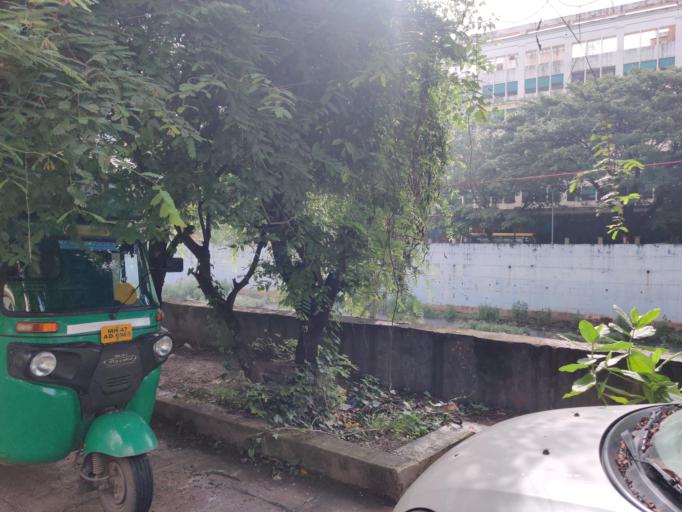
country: IN
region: Maharashtra
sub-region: Mumbai Suburban
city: Borivli
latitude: 19.2436
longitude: 72.8566
